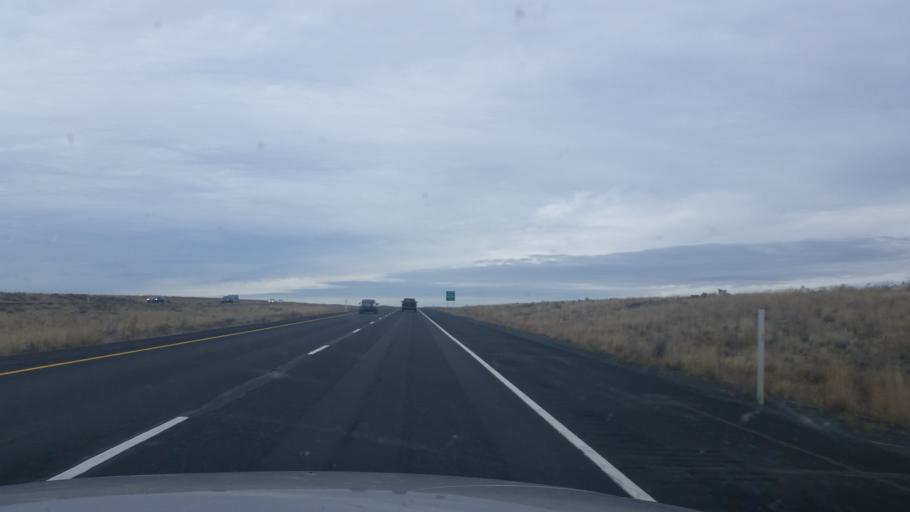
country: US
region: Washington
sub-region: Adams County
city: Ritzville
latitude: 47.1115
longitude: -118.4647
